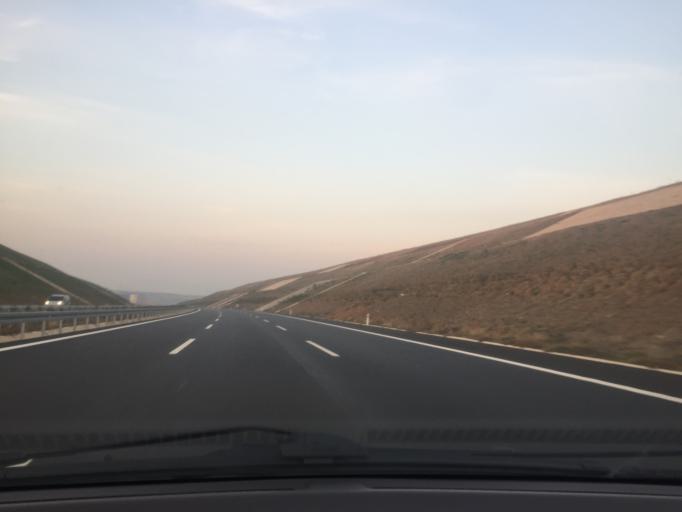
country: TR
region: Bursa
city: Mahmudiye
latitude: 40.2774
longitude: 28.5390
